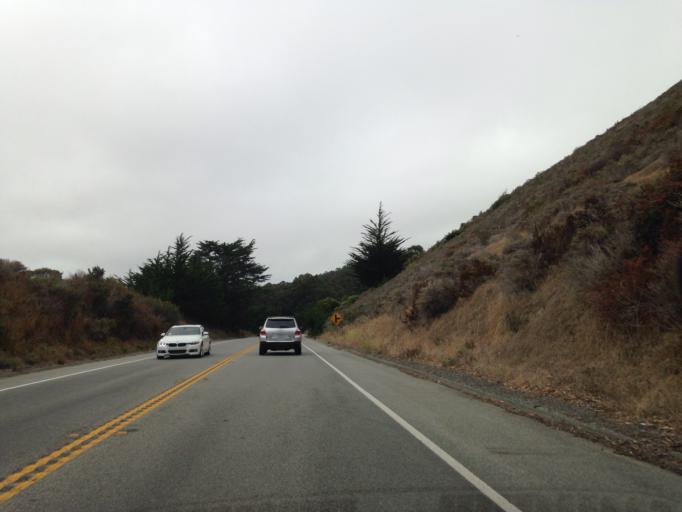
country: US
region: California
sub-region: San Mateo County
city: Half Moon Bay
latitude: 37.3790
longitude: -122.4042
